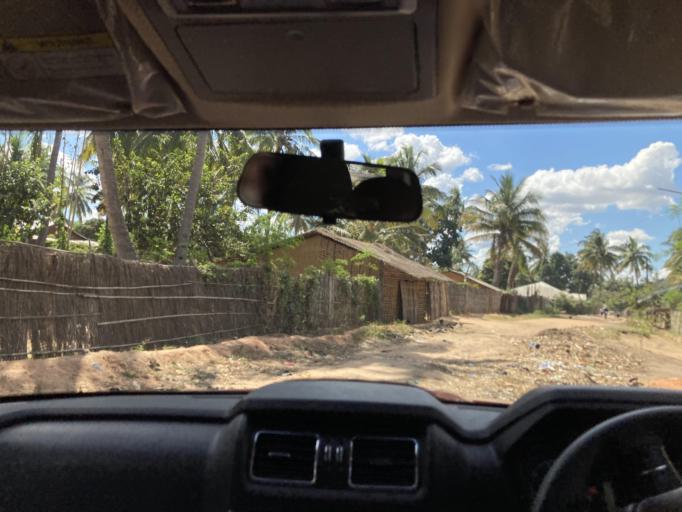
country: MZ
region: Cabo Delgado
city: Montepuez
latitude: -13.1373
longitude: 39.0017
